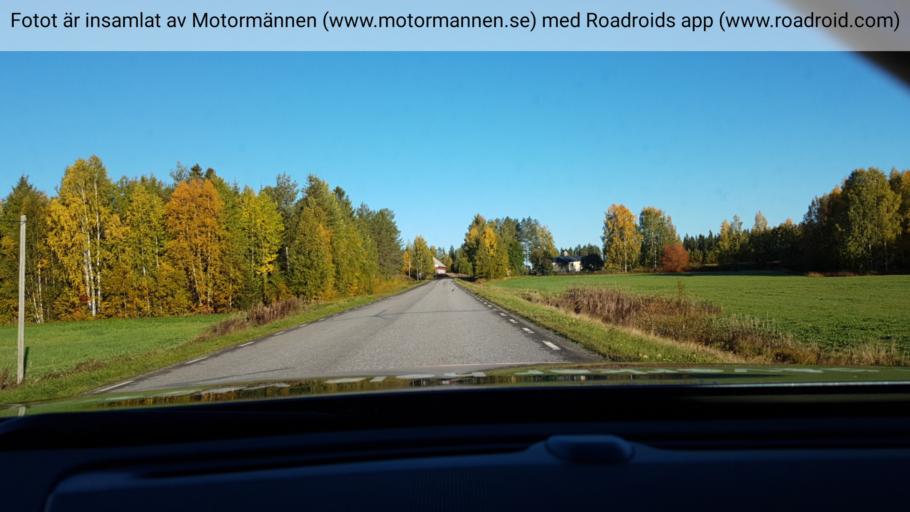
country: SE
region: Norrbotten
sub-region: Bodens Kommun
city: Boden
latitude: 65.8995
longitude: 21.6727
